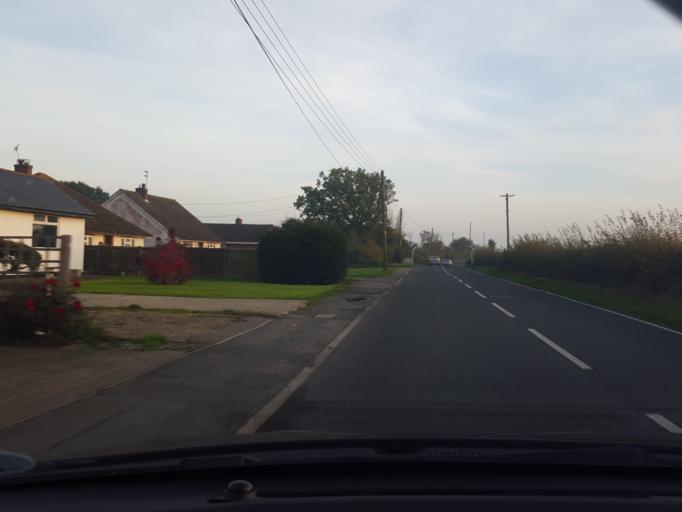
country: GB
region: England
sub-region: Essex
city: Little Clacton
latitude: 51.8398
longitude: 1.1537
